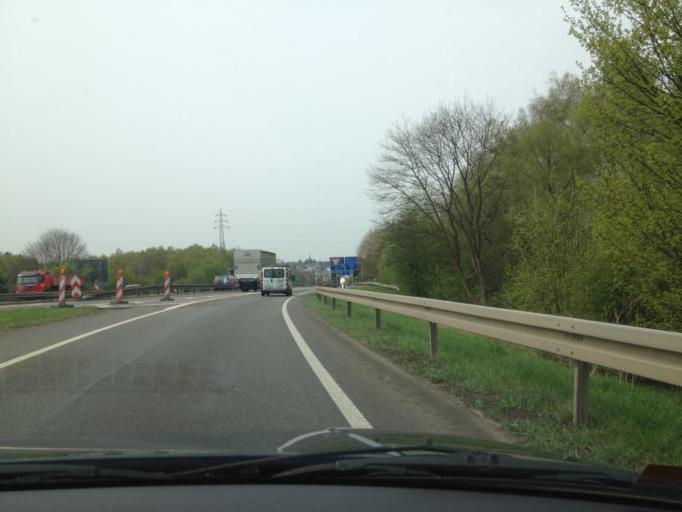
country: DE
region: Saarland
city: Spiesen-Elversberg
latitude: 49.3245
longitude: 7.1571
